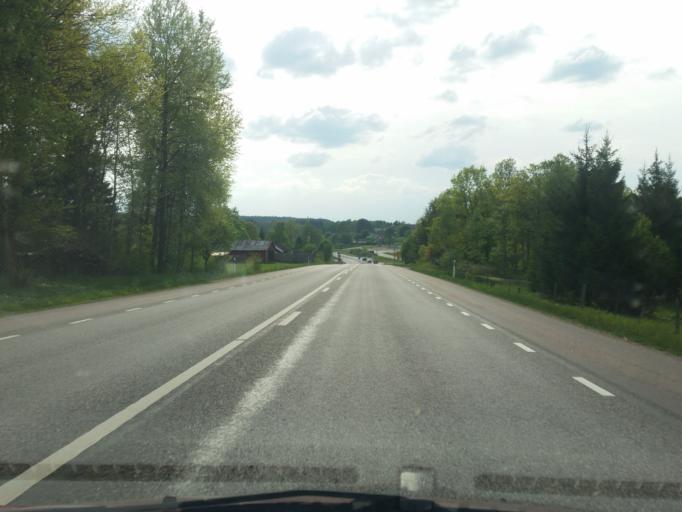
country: SE
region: Vaestra Goetaland
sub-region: Ulricehamns Kommun
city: Ulricehamn
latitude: 57.8092
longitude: 13.2625
